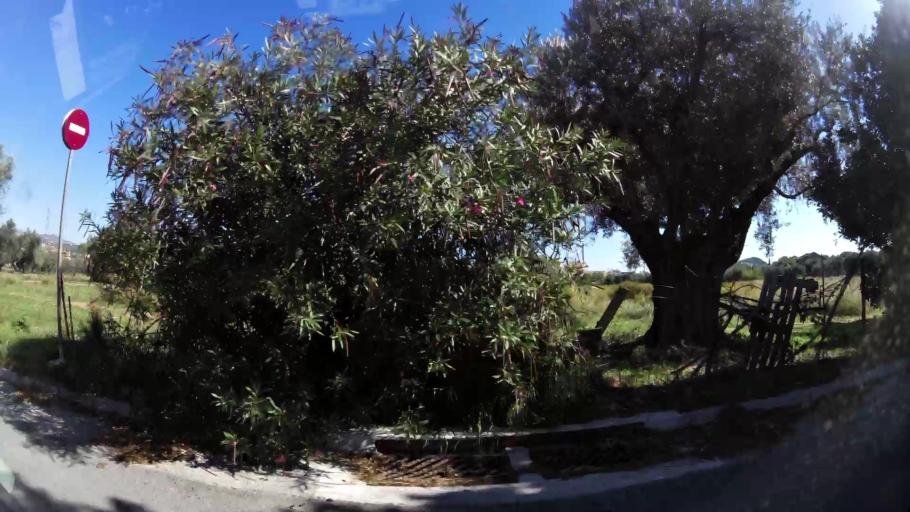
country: GR
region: Attica
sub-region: Nomarchia Anatolikis Attikis
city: Leondarion
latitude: 37.9895
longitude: 23.8636
